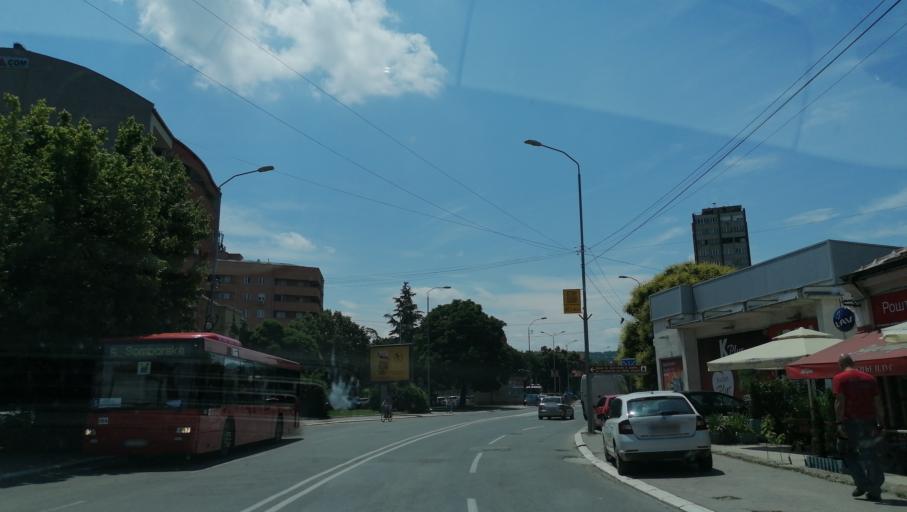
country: RS
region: Central Serbia
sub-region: Nisavski Okrug
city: Nis
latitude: 43.3250
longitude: 21.9029
